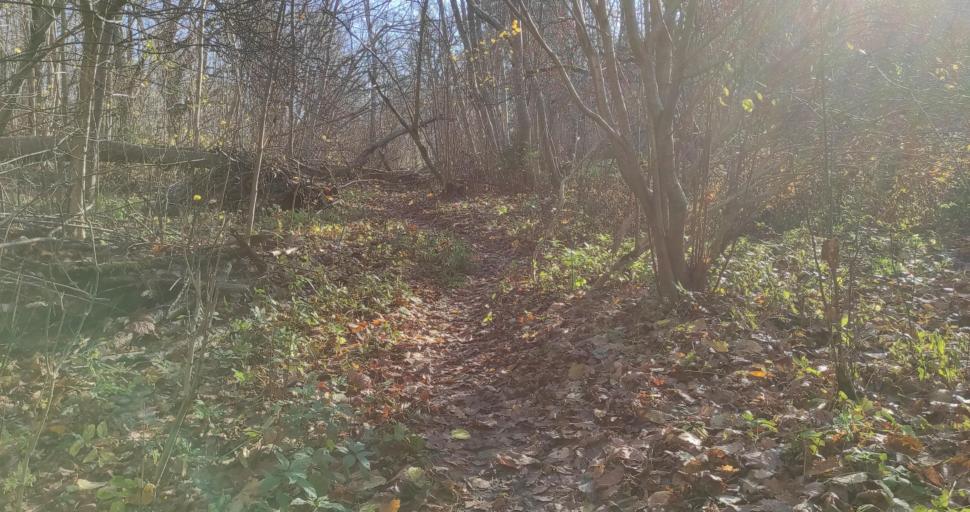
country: LV
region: Saldus Rajons
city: Saldus
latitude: 56.6643
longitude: 22.5205
